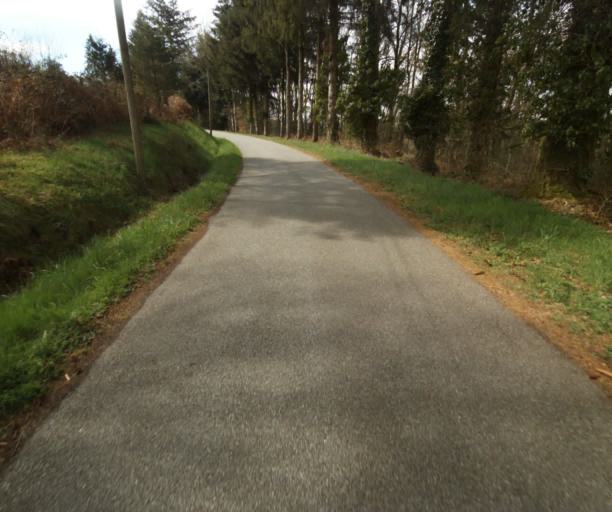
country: FR
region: Limousin
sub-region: Departement de la Correze
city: Correze
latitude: 45.3842
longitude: 1.8944
